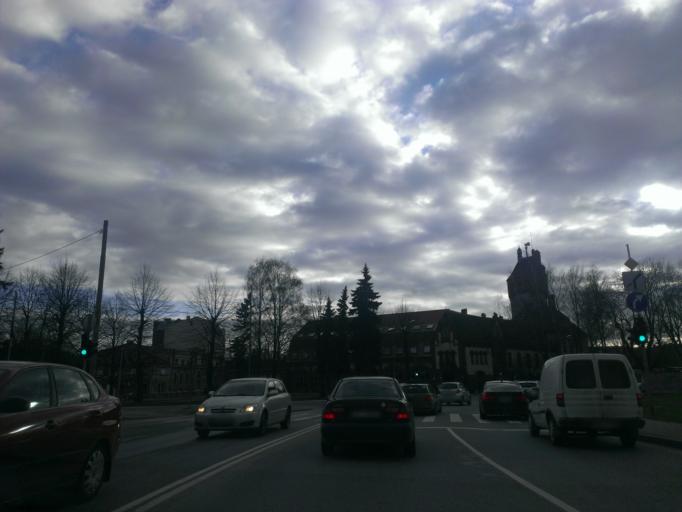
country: LV
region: Riga
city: Riga
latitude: 56.9629
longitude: 24.1136
